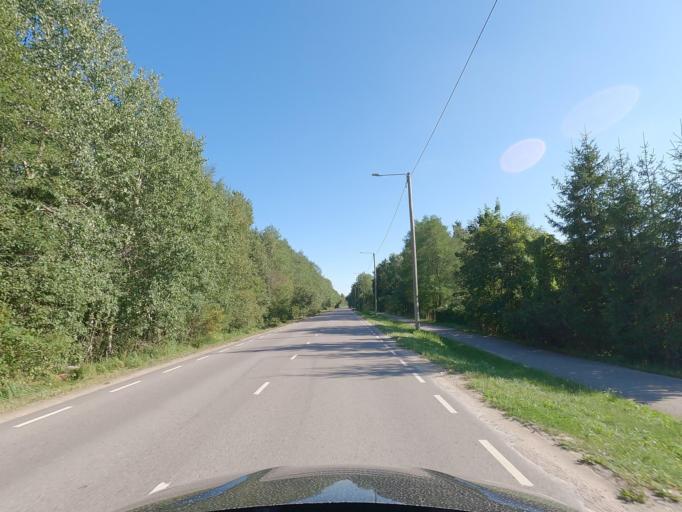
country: EE
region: Harju
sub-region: Saku vald
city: Saku
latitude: 59.2074
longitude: 24.6645
